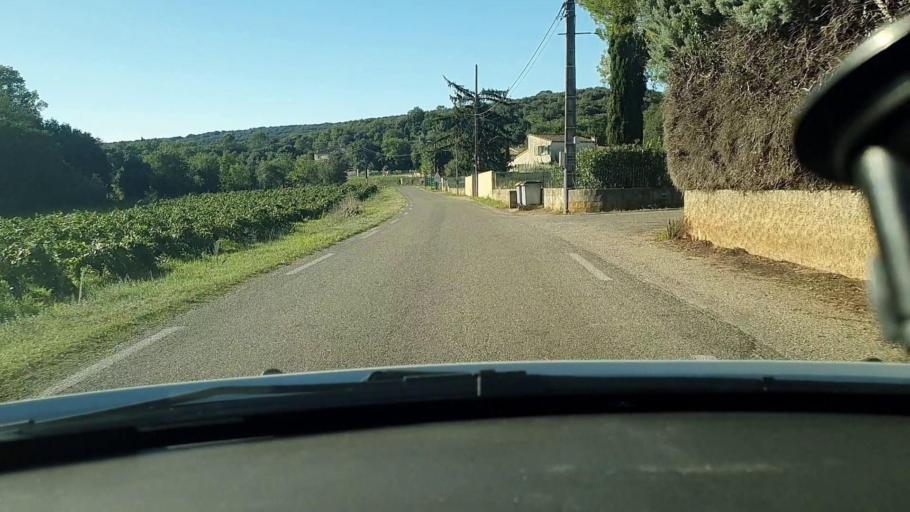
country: FR
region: Languedoc-Roussillon
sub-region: Departement du Gard
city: Goudargues
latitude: 44.2343
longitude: 4.4426
